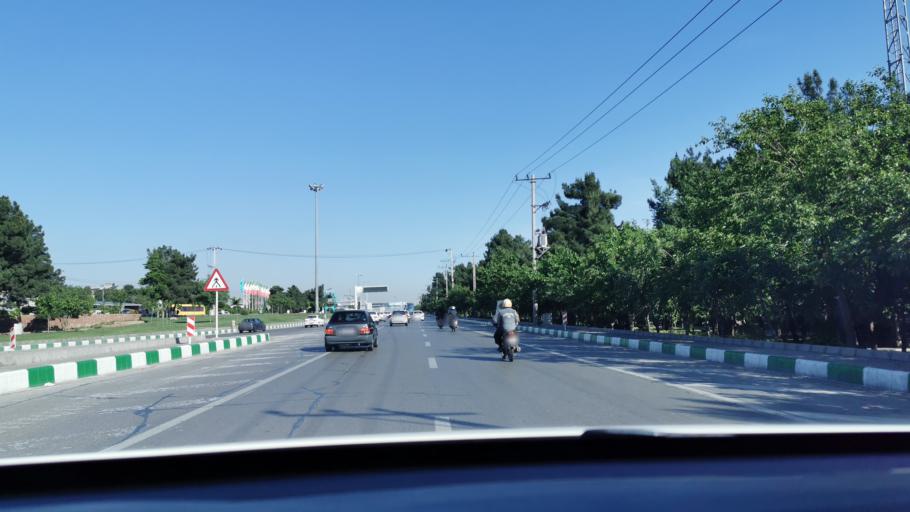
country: IR
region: Razavi Khorasan
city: Mashhad
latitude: 36.2518
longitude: 59.6077
